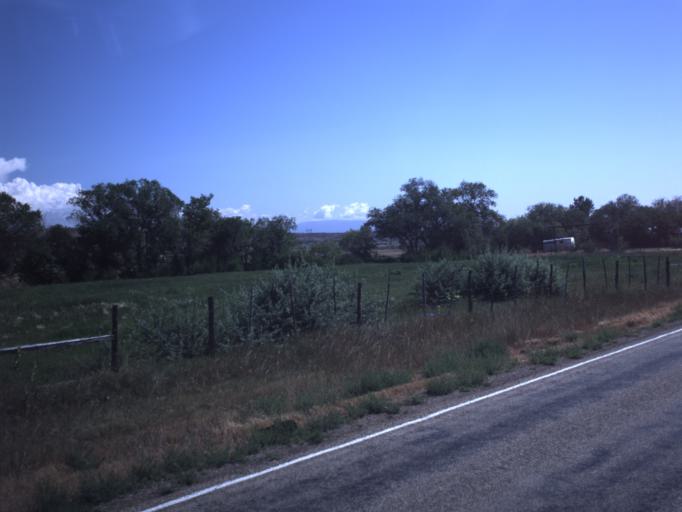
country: US
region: Utah
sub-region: Duchesne County
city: Roosevelt
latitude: 40.2580
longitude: -110.1556
